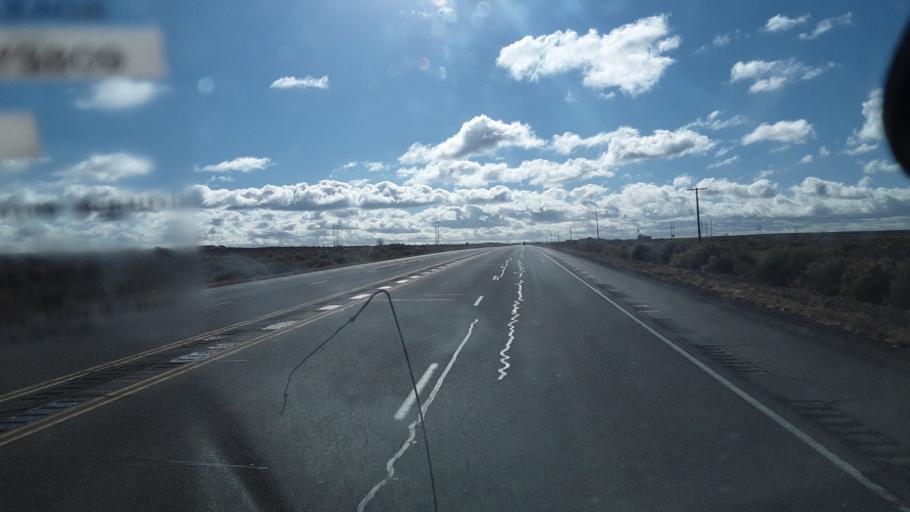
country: US
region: New Mexico
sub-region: San Juan County
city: Lee Acres
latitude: 36.5877
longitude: -108.0021
